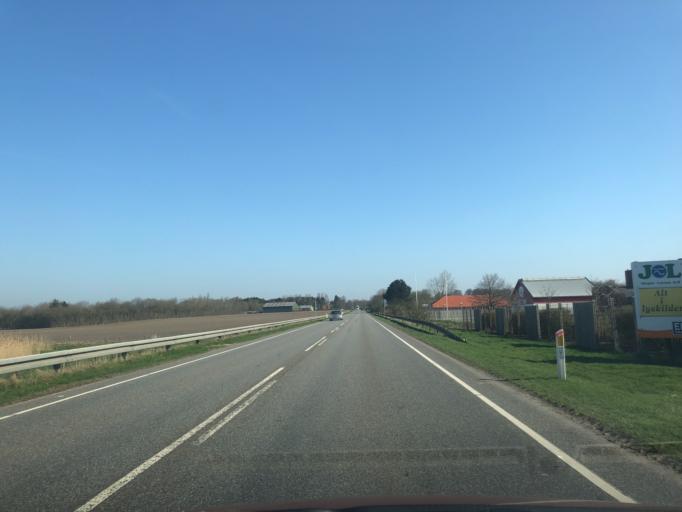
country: DK
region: Zealand
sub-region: Faxe Kommune
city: Haslev
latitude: 55.3305
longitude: 11.9420
